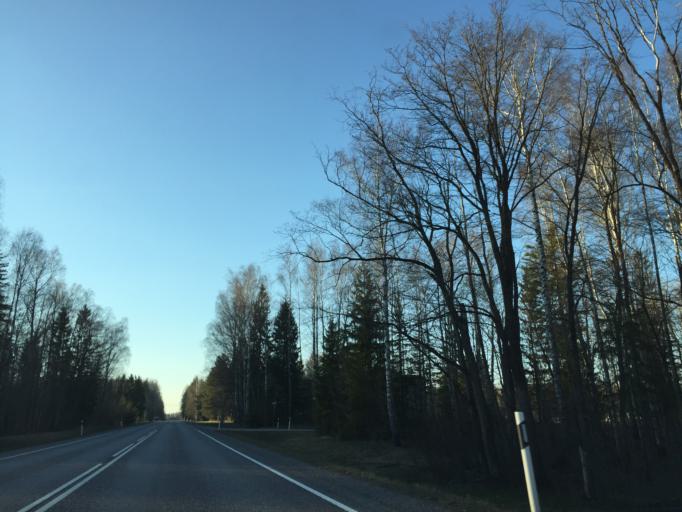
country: EE
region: Ida-Virumaa
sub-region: Johvi vald
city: Johvi
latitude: 59.3246
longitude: 27.4864
